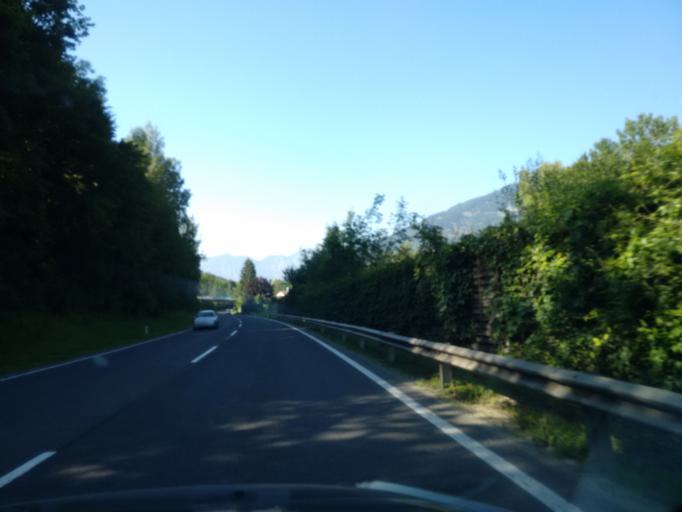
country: AT
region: Upper Austria
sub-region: Politischer Bezirk Gmunden
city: Bad Ischl
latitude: 47.7095
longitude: 13.6294
